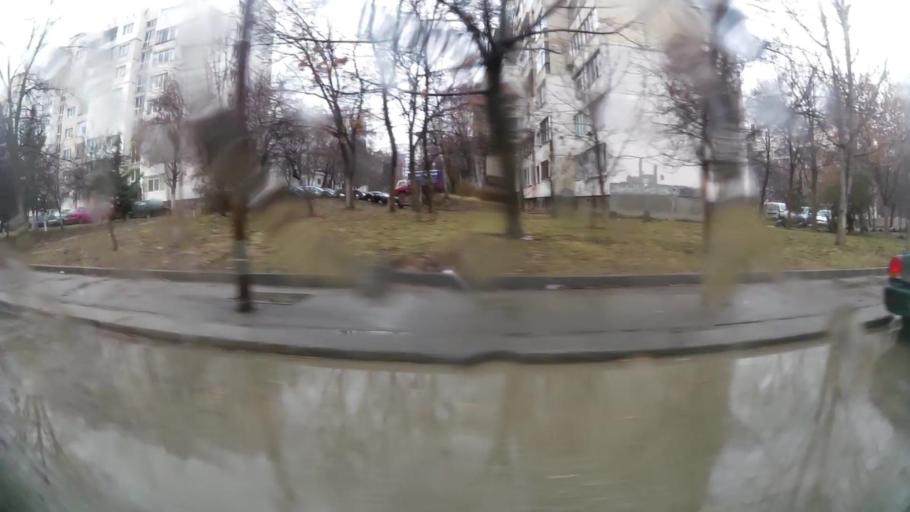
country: BG
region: Sofia-Capital
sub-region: Stolichna Obshtina
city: Sofia
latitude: 42.6546
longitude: 23.3650
